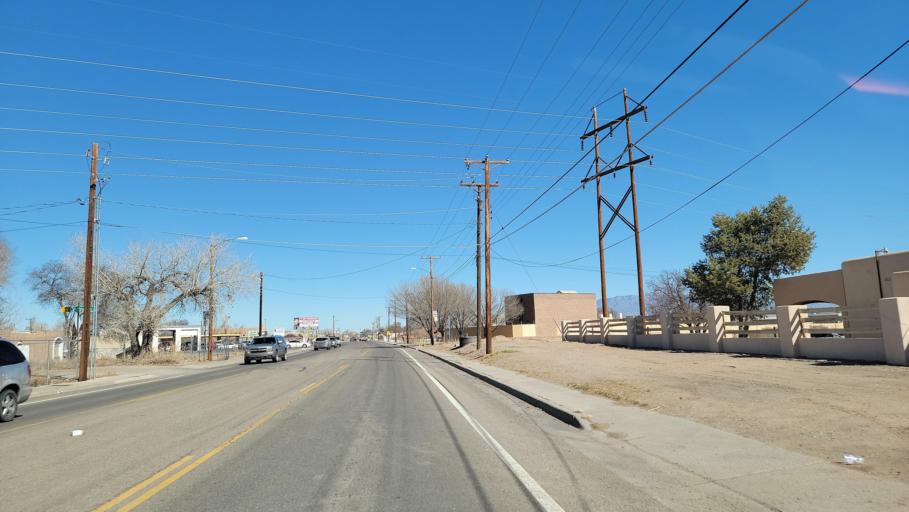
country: US
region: New Mexico
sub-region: Bernalillo County
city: South Valley
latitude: 35.0160
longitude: -106.6849
